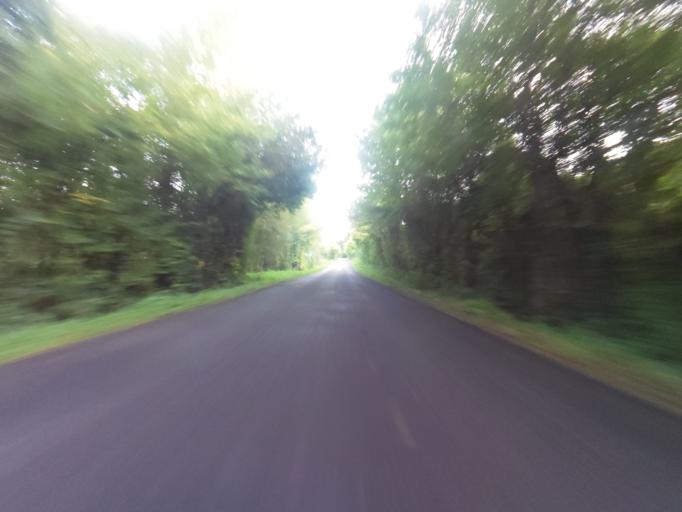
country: FR
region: Lower Normandy
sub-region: Departement de l'Orne
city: Vimoutiers
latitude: 48.9547
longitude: 0.2641
